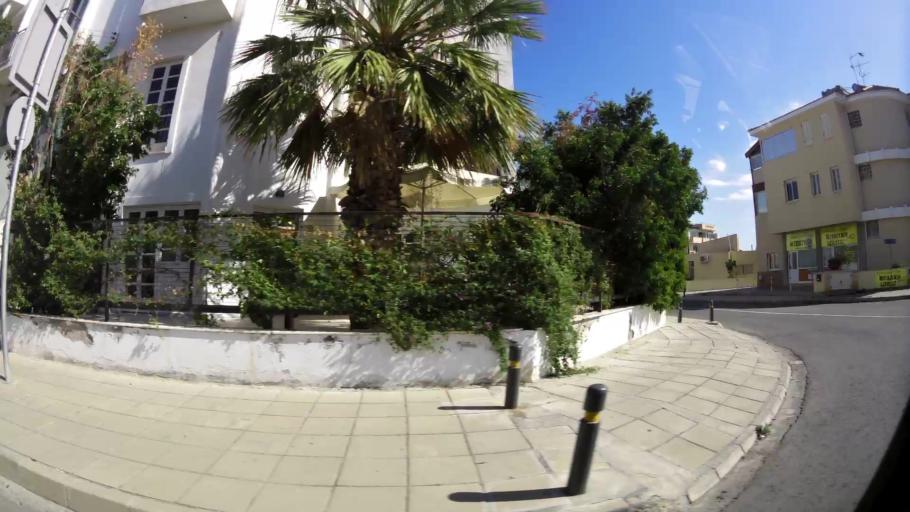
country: CY
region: Lefkosia
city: Nicosia
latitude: 35.1406
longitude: 33.3629
